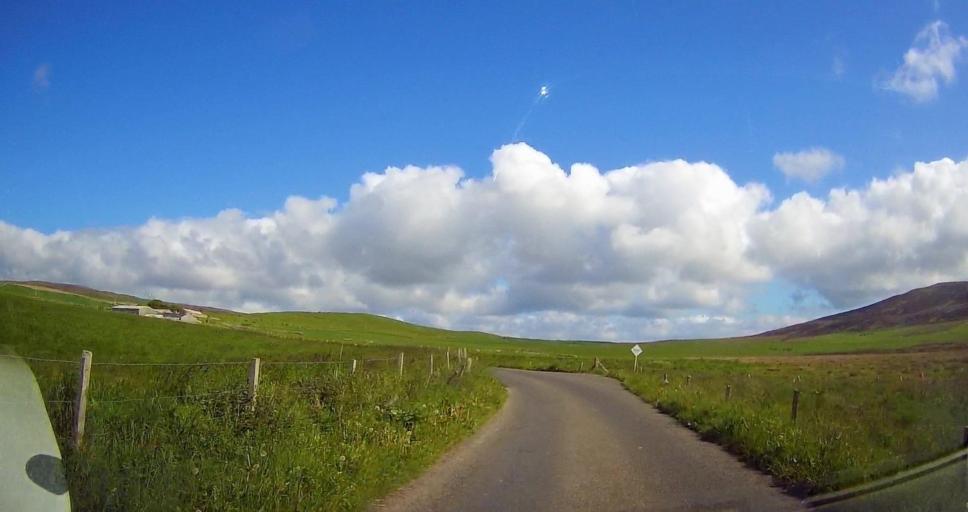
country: GB
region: Scotland
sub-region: Orkney Islands
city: Stromness
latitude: 58.9841
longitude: -3.1469
